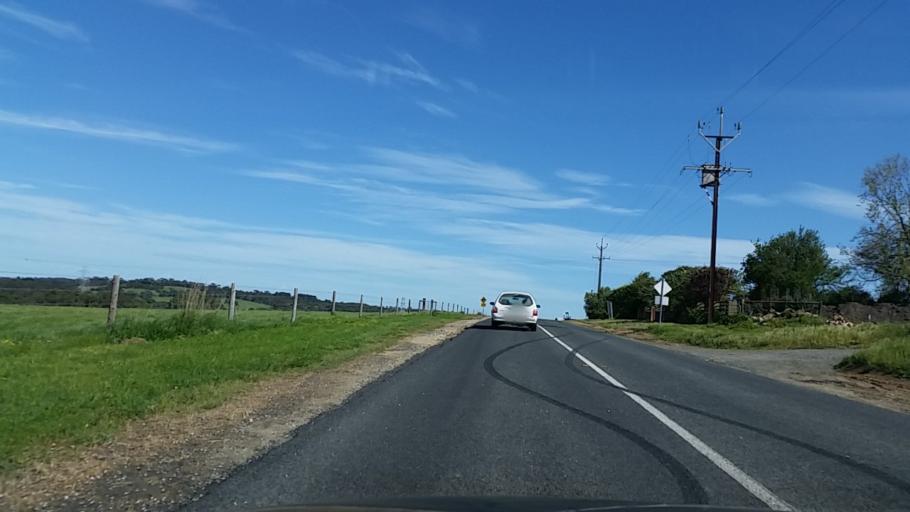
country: AU
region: South Australia
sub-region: Mount Barker
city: Little Hampton
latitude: -35.0754
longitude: 138.8337
